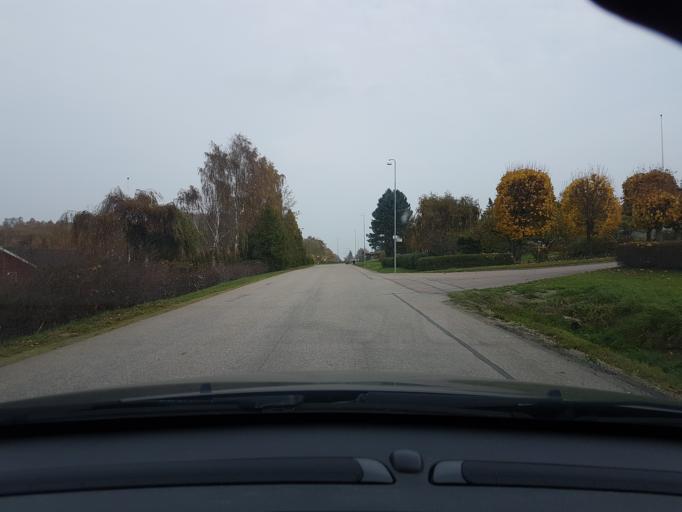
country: SE
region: Vaestra Goetaland
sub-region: Ale Kommun
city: Alvangen
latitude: 57.9469
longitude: 12.1034
